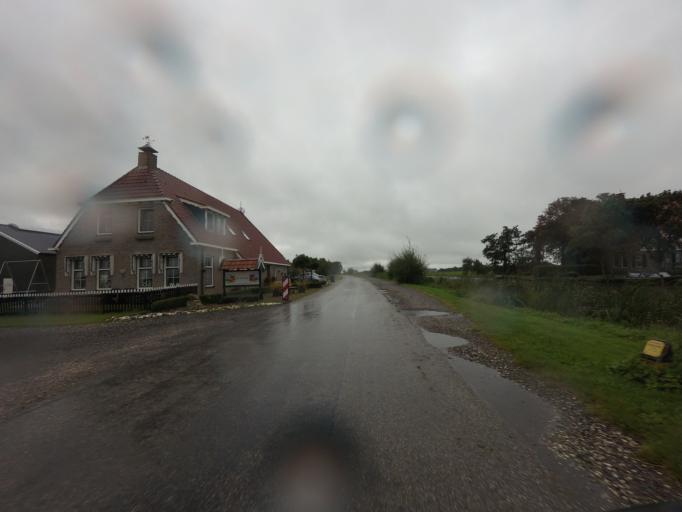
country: NL
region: Friesland
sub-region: Sudwest Fryslan
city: Workum
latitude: 52.9974
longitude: 5.4745
